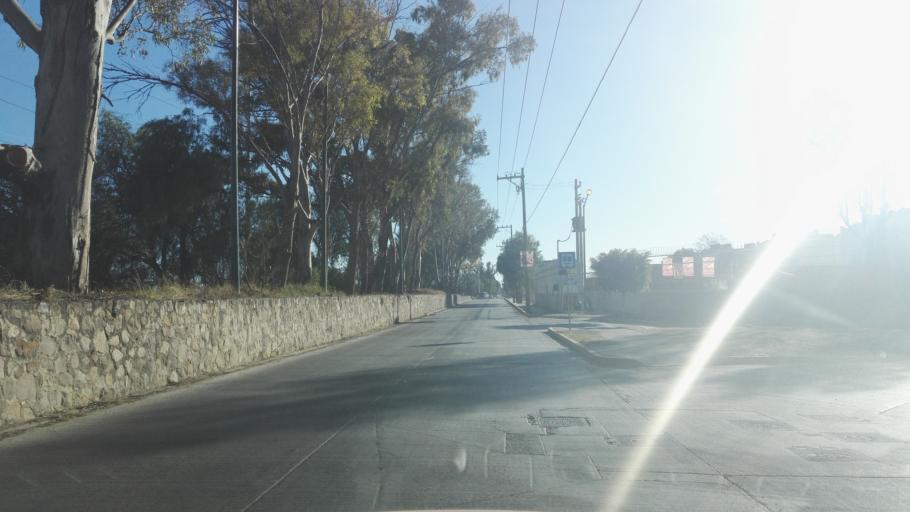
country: MX
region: Guanajuato
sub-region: Leon
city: Fraccionamiento Paraiso Real
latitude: 21.0654
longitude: -101.6056
